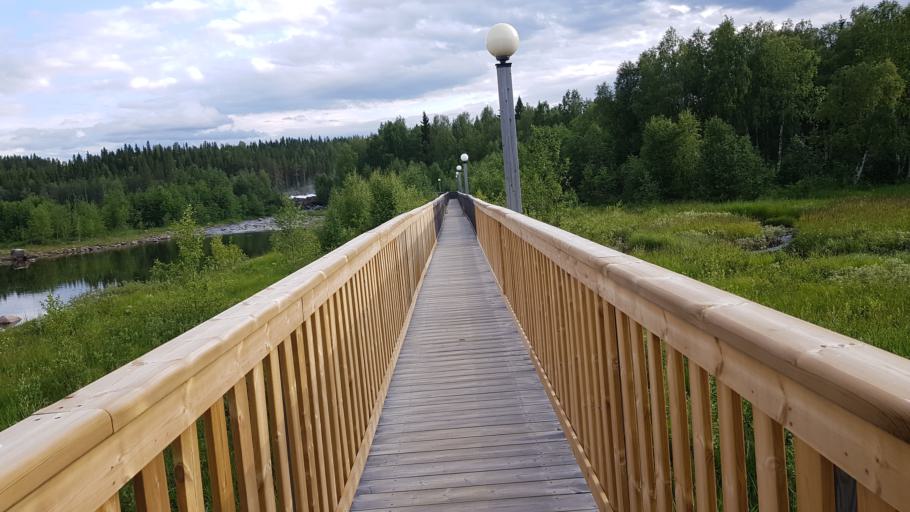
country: SE
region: Norrbotten
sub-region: Alvsbyns Kommun
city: AElvsbyn
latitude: 65.8561
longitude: 20.4168
